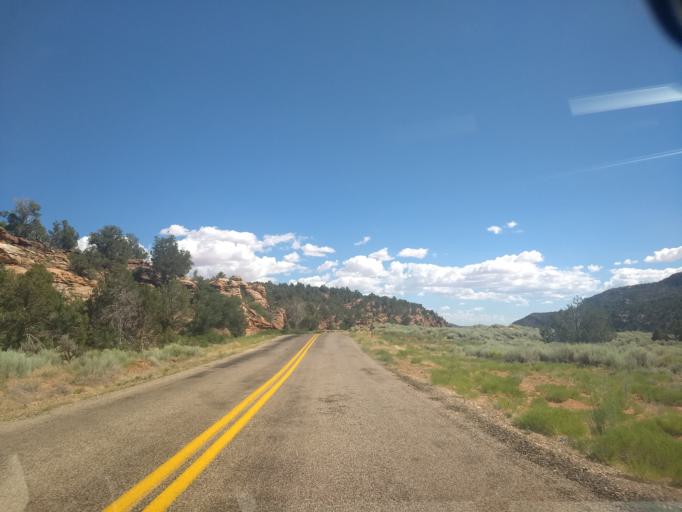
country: US
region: Utah
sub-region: Washington County
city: Hildale
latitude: 36.9884
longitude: -112.8686
